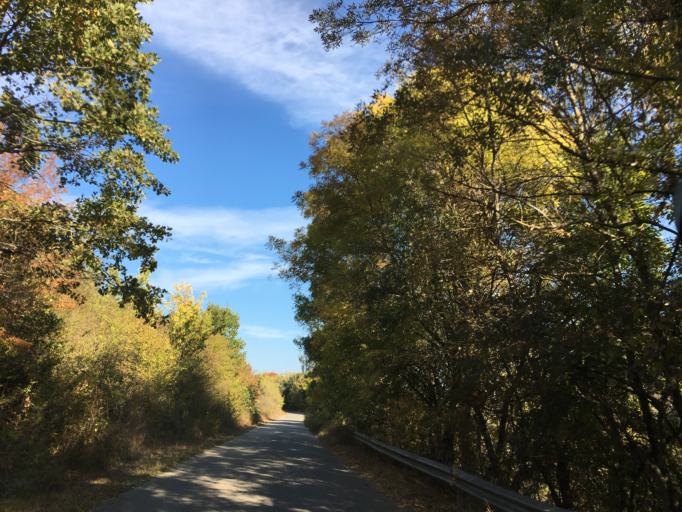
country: BG
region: Khaskovo
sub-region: Obshtina Ivaylovgrad
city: Ivaylovgrad
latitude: 41.3963
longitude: 26.1273
